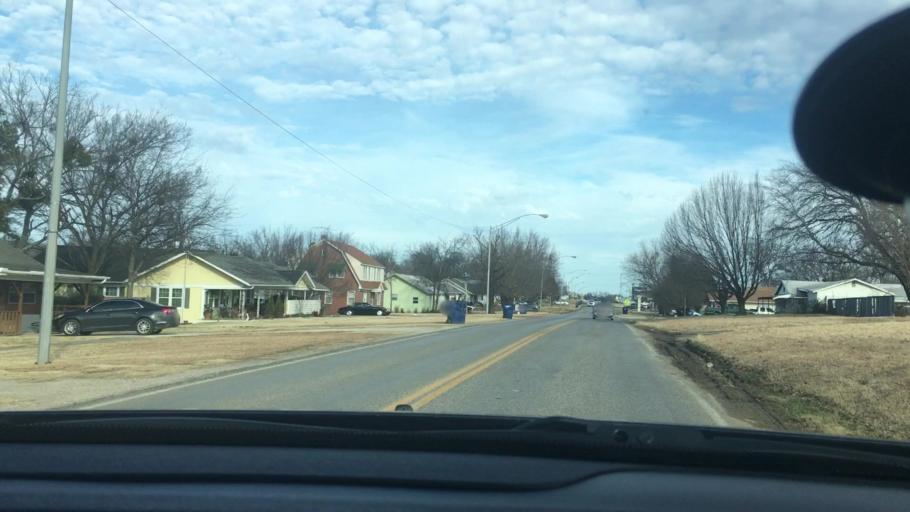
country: US
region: Oklahoma
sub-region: Seminole County
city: Konawa
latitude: 34.9528
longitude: -96.7521
